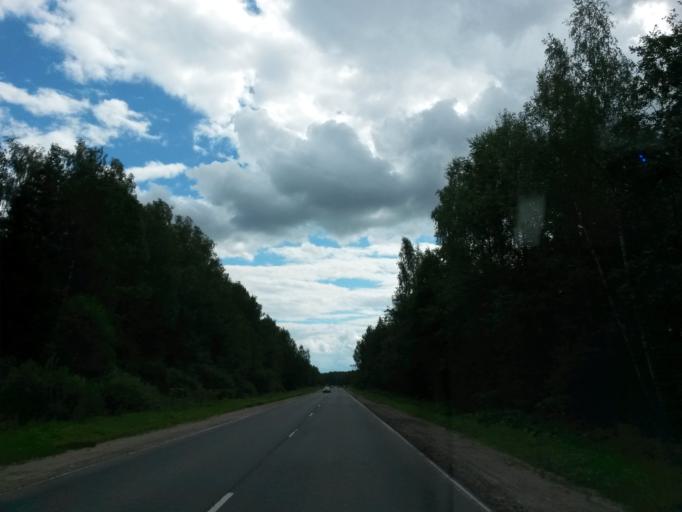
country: RU
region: Ivanovo
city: Pistsovo
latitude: 57.1002
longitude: 40.6556
